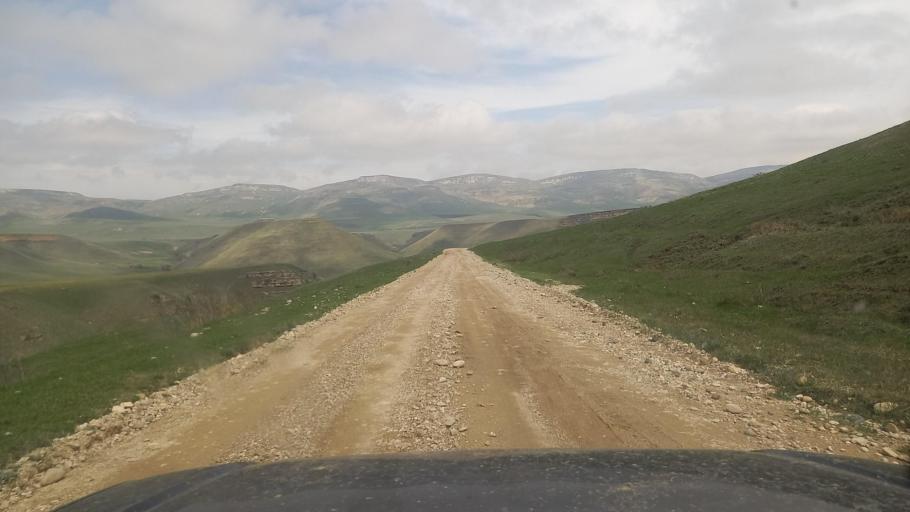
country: RU
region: Stavropol'skiy
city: Kislovodsk
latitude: 43.7962
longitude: 42.8667
